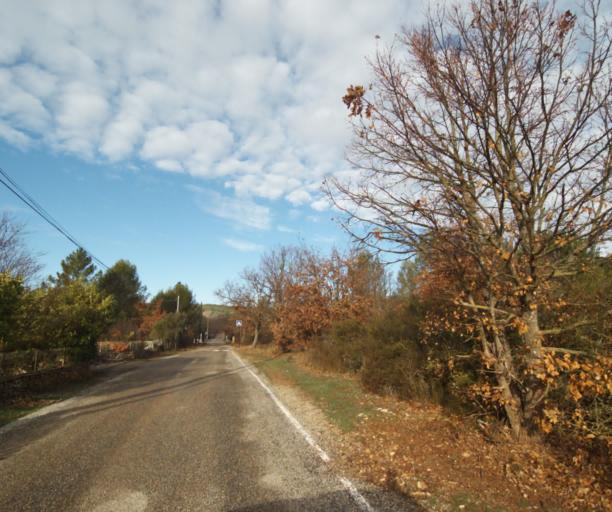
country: FR
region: Provence-Alpes-Cote d'Azur
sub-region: Departement du Var
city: Trans-en-Provence
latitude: 43.4903
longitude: 6.4738
